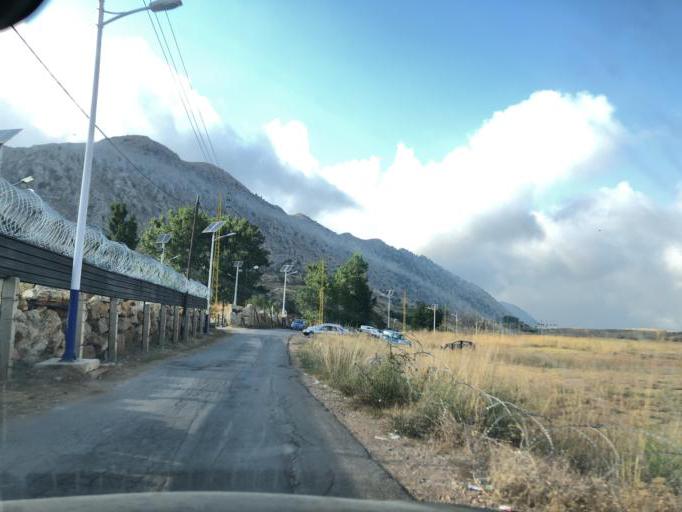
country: LB
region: Liban-Nord
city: Amioun
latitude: 34.1452
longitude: 35.8591
